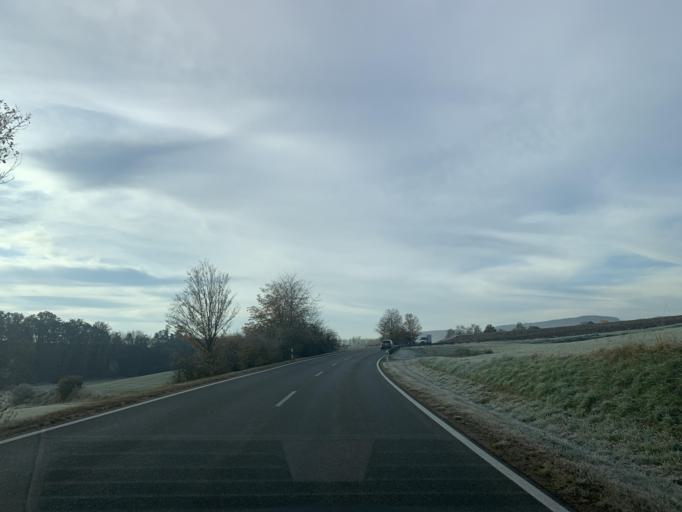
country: DE
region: Bavaria
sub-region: Upper Palatinate
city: Neunburg vorm Wald
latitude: 49.3649
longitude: 12.3788
